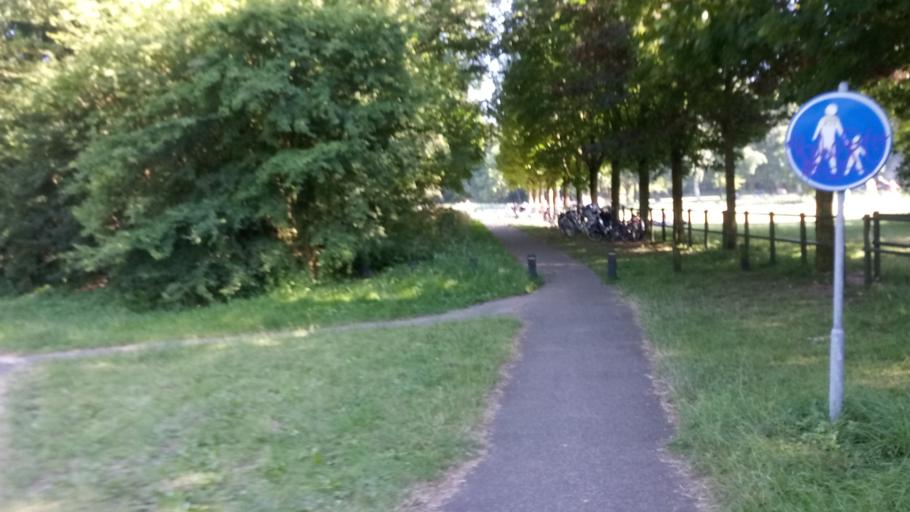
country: NL
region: Gelderland
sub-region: Gemeente Voorst
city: Twello
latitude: 52.2040
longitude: 6.1108
